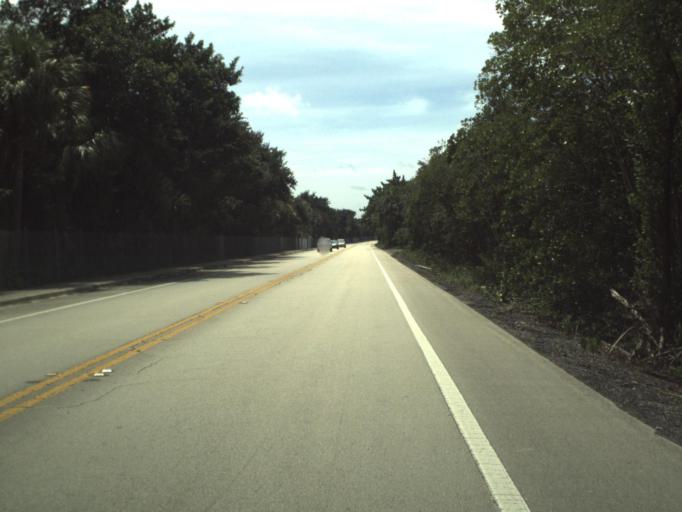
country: US
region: Florida
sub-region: Palm Beach County
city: Lake Park
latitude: 26.8301
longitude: -80.0471
